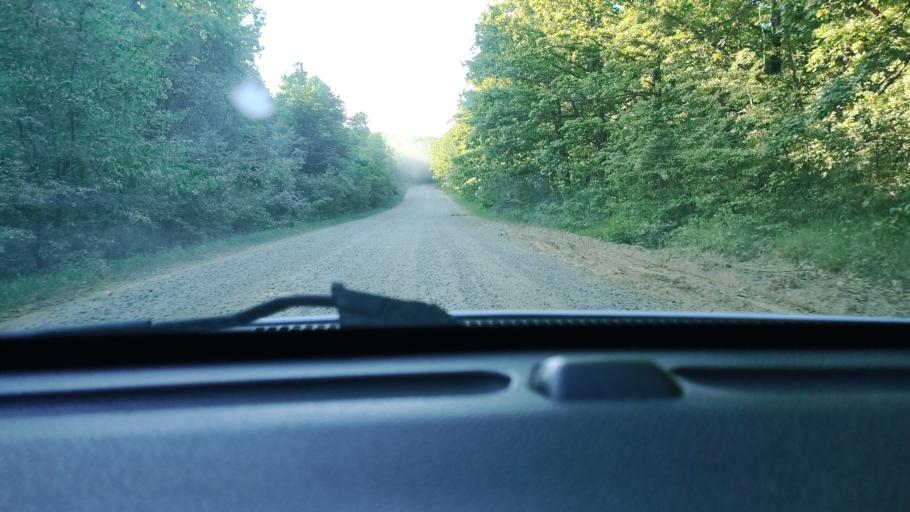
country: RU
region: Krasnodarskiy
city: Goryachiy Klyuch
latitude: 44.7108
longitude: 38.9921
